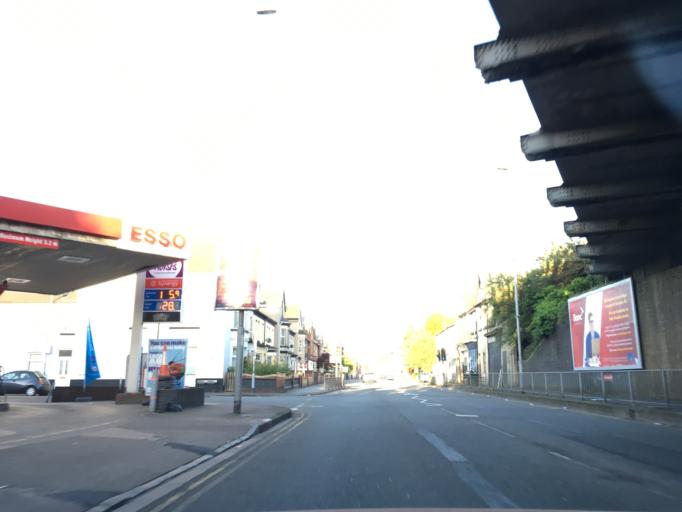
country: GB
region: Wales
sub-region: Newport
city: Newport
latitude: 51.5906
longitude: -2.9843
